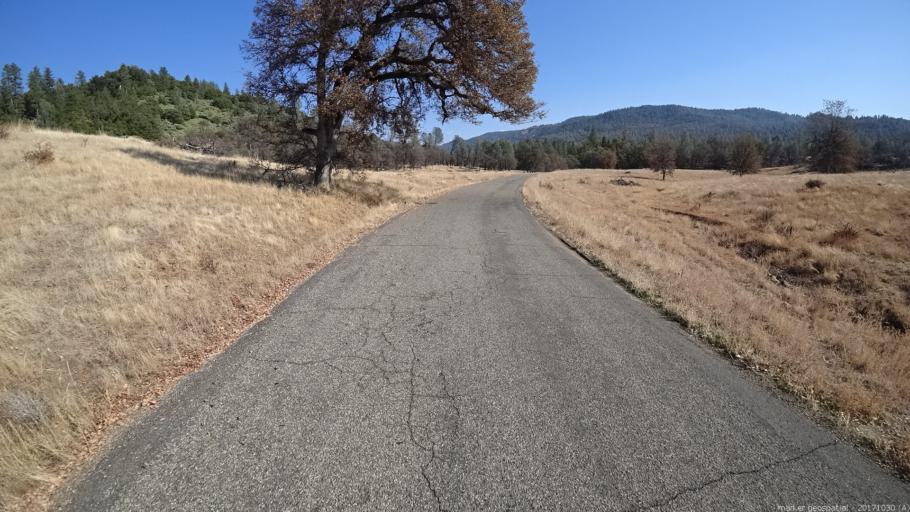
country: US
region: California
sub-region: Shasta County
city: Shingletown
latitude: 40.5391
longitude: -121.9282
